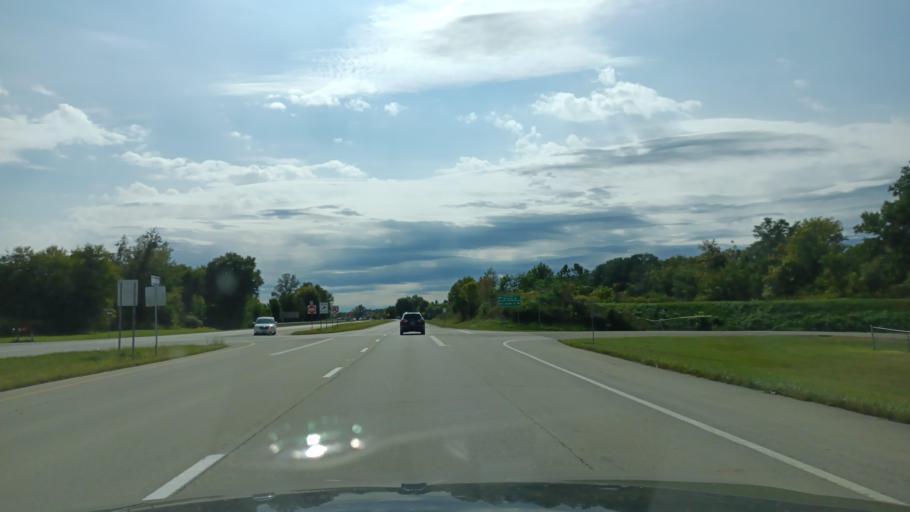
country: US
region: Ohio
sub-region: Athens County
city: Athens
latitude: 39.2408
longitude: -82.1899
